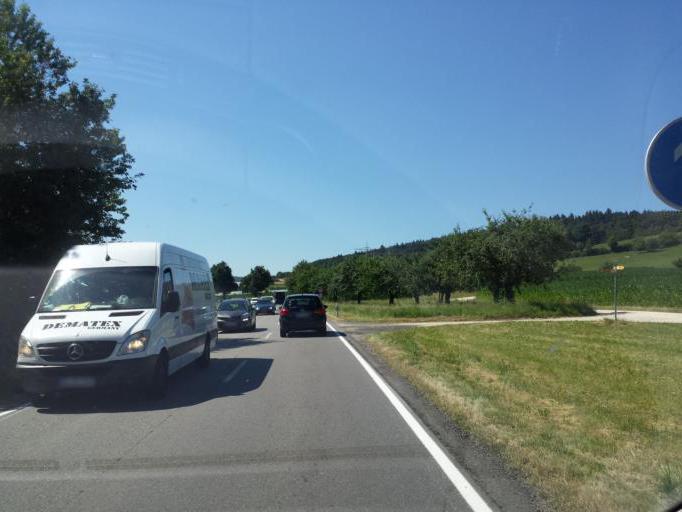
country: DE
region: Baden-Wuerttemberg
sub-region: Tuebingen Region
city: Owingen
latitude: 47.7908
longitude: 9.1605
